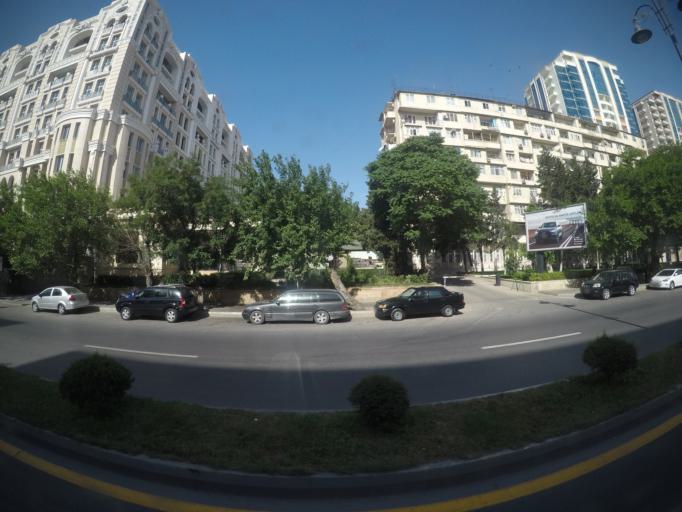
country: AZ
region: Baki
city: Badamdar
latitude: 40.3881
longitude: 49.8239
